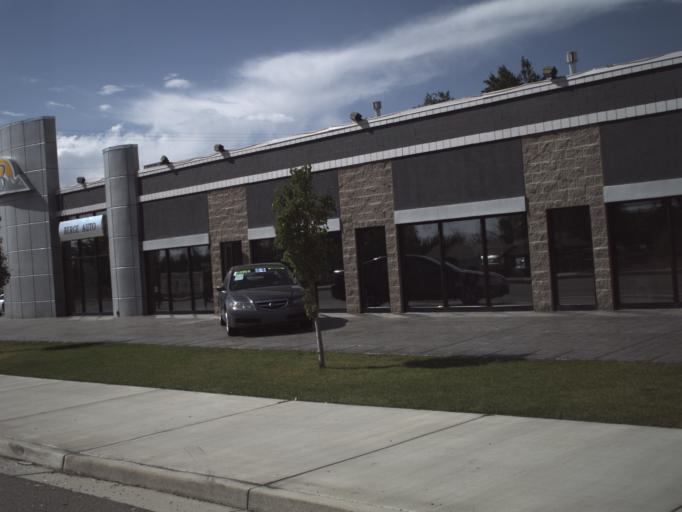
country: US
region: Utah
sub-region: Utah County
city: Orem
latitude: 40.3121
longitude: -111.6885
